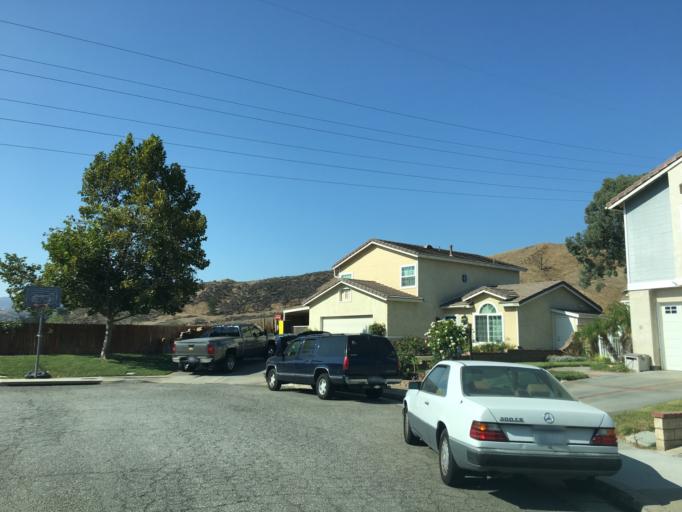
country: US
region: California
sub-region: Los Angeles County
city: Valencia
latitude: 34.4479
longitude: -118.6193
